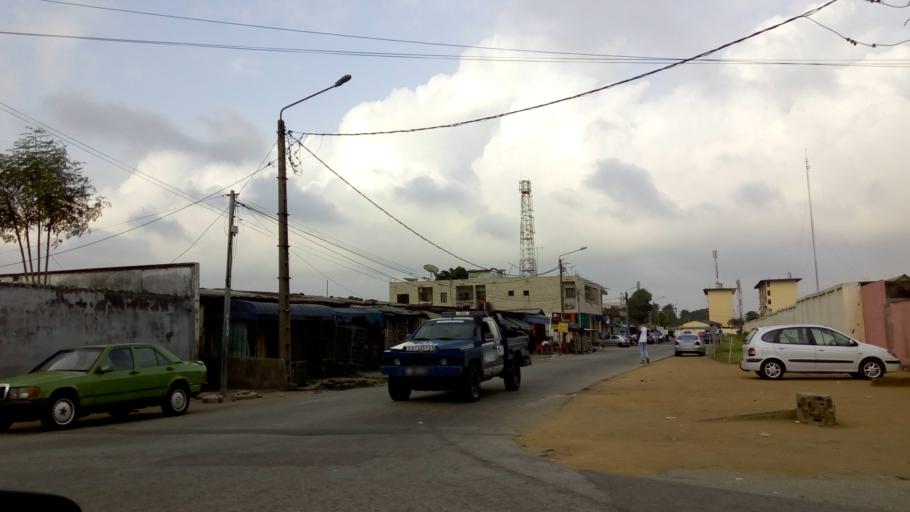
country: CI
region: Lagunes
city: Abidjan
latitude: 5.3382
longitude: -4.0259
